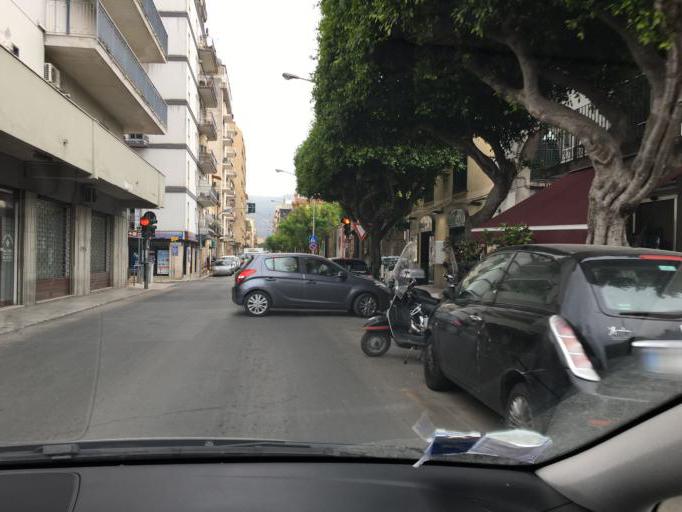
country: IT
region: Sicily
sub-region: Palermo
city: Palermo
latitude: 38.1110
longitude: 13.3397
